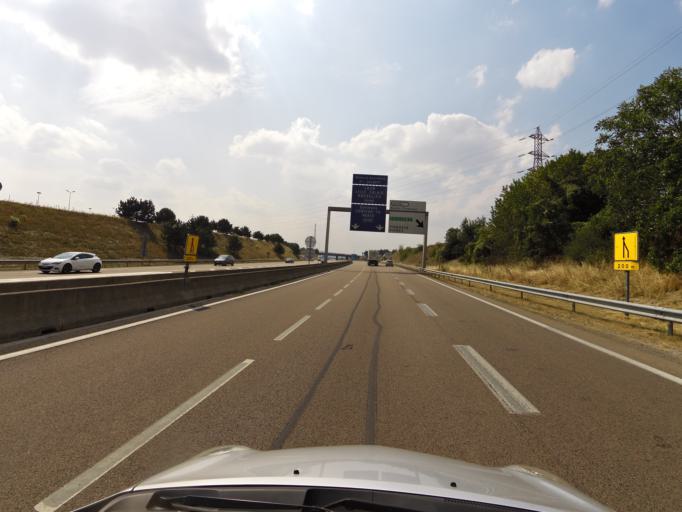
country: FR
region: Champagne-Ardenne
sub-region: Departement de la Marne
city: Tinqueux
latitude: 49.2558
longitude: 3.9786
